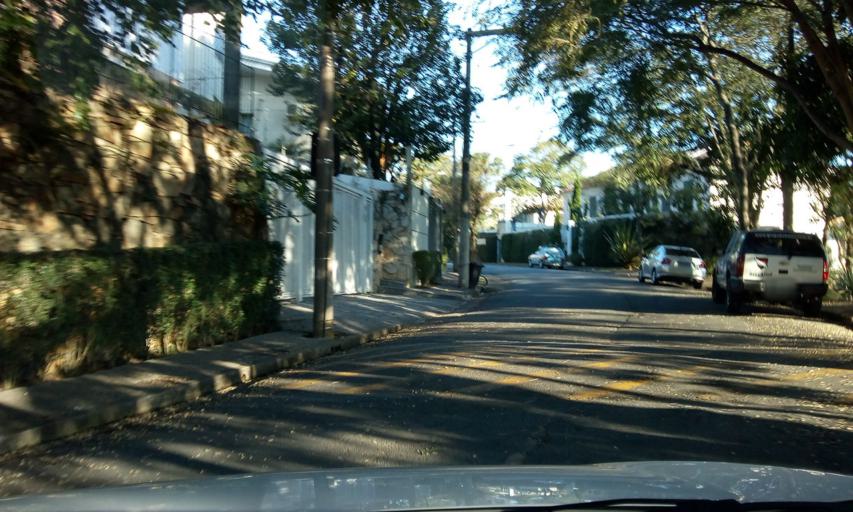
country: BR
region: Sao Paulo
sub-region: Sao Paulo
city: Sao Paulo
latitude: -23.5952
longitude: -46.7020
